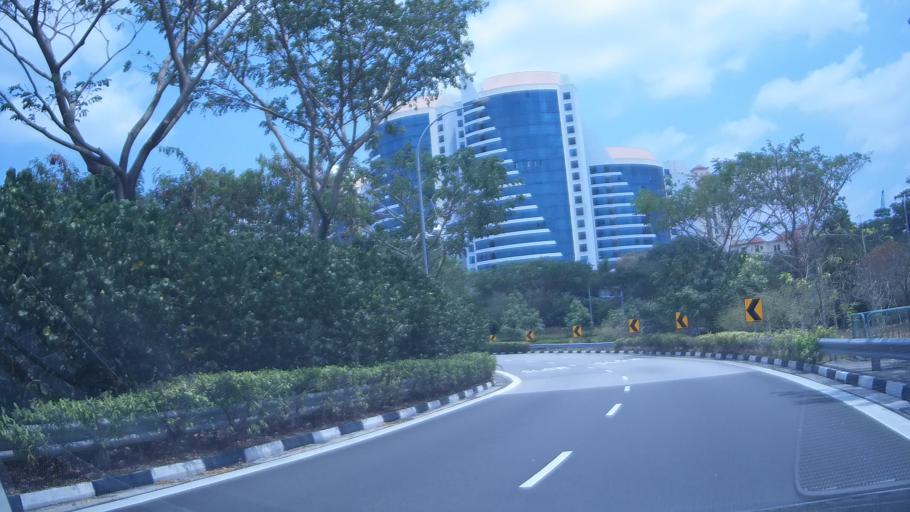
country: SG
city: Singapore
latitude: 1.2946
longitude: 103.8739
